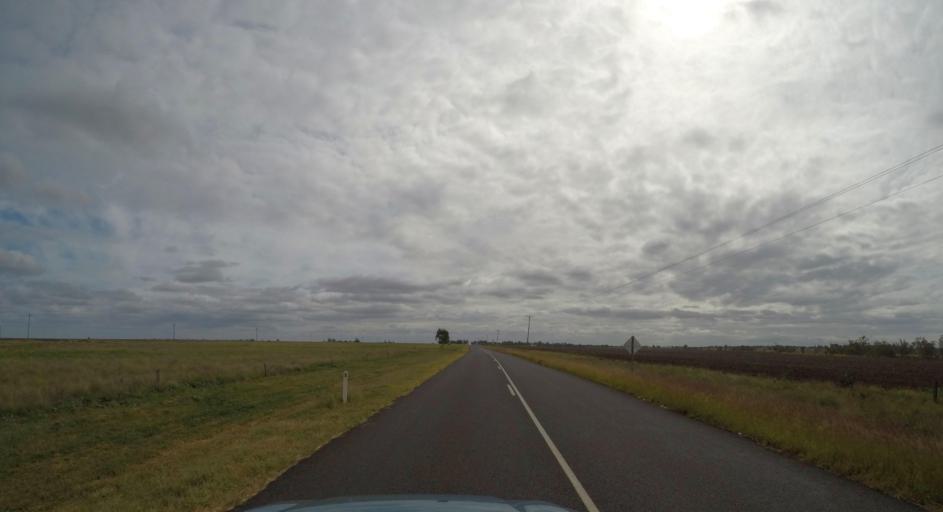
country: AU
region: Queensland
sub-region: Western Downs
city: Dalby
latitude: -26.9799
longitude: 151.2241
